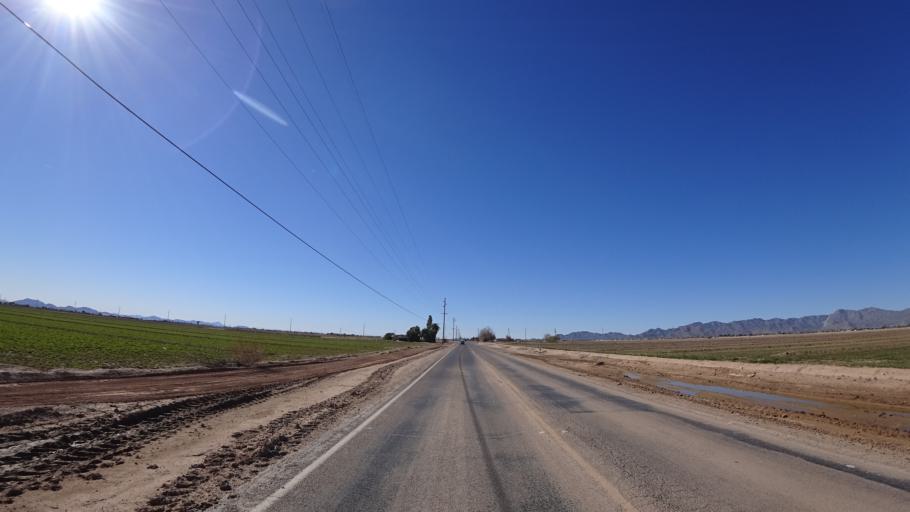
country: US
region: Arizona
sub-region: Maricopa County
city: Goodyear
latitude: 33.4357
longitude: -112.4502
